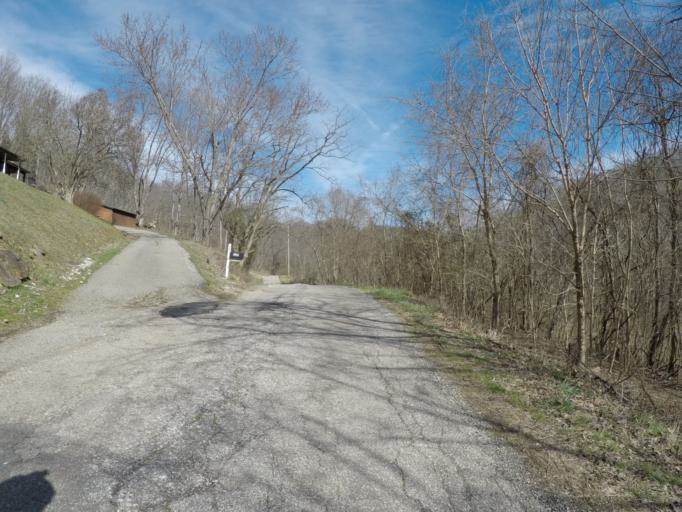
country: US
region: West Virginia
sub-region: Wayne County
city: Ceredo
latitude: 38.3475
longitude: -82.5596
